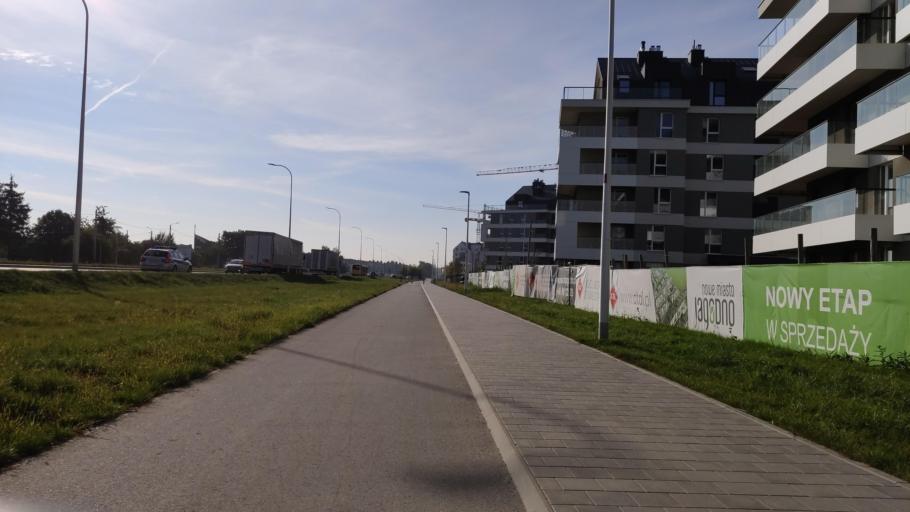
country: PL
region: Lower Silesian Voivodeship
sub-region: Powiat wroclawski
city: Zerniki Wroclawskie
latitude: 51.0606
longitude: 17.0552
